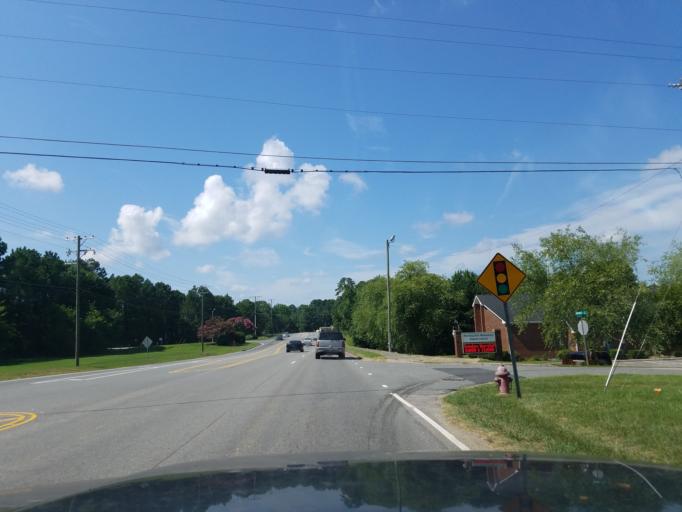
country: US
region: North Carolina
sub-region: Durham County
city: Durham
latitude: 35.9383
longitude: -78.9075
